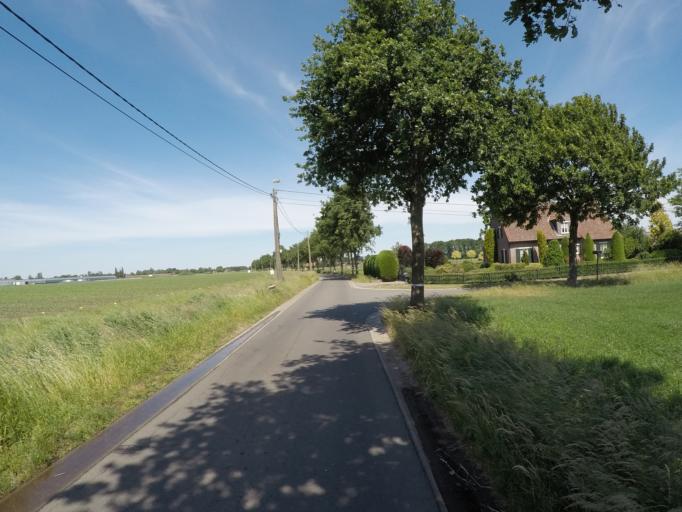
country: NL
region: North Brabant
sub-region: Gemeente Zundert
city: Zundert
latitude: 51.4117
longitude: 4.6532
